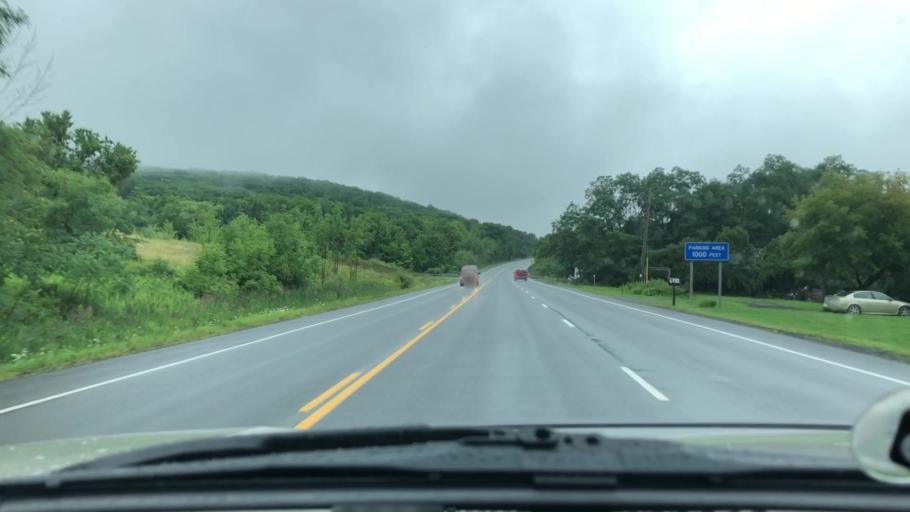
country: US
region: New York
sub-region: Greene County
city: Cairo
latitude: 42.3378
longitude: -74.1247
